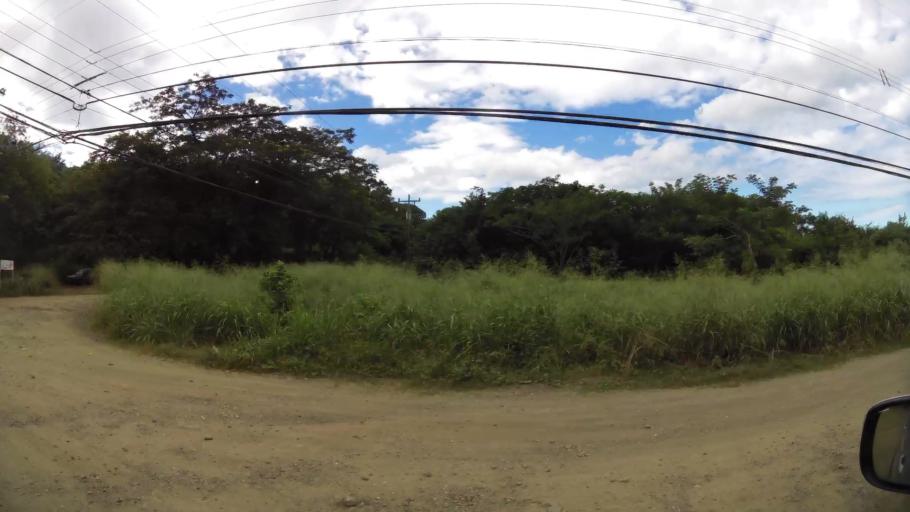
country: CR
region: Guanacaste
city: Santa Cruz
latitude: 10.3029
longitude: -85.8371
